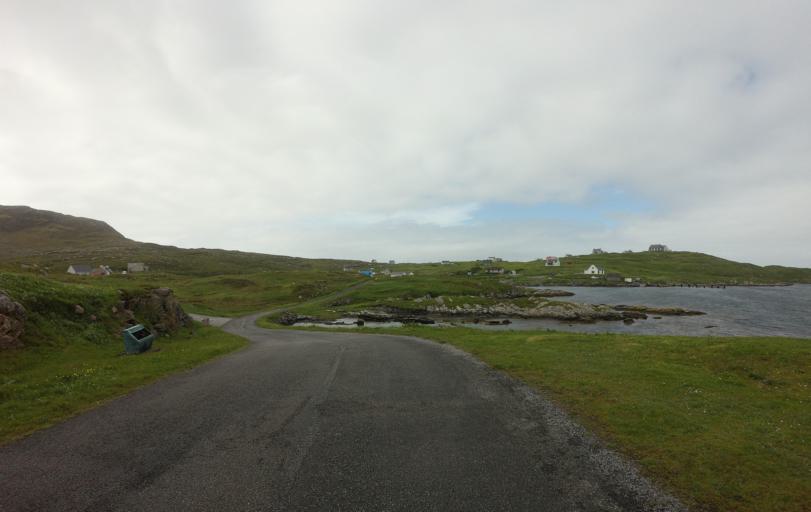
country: GB
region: Scotland
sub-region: Eilean Siar
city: Isle of South Uist
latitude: 57.0877
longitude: -7.2985
